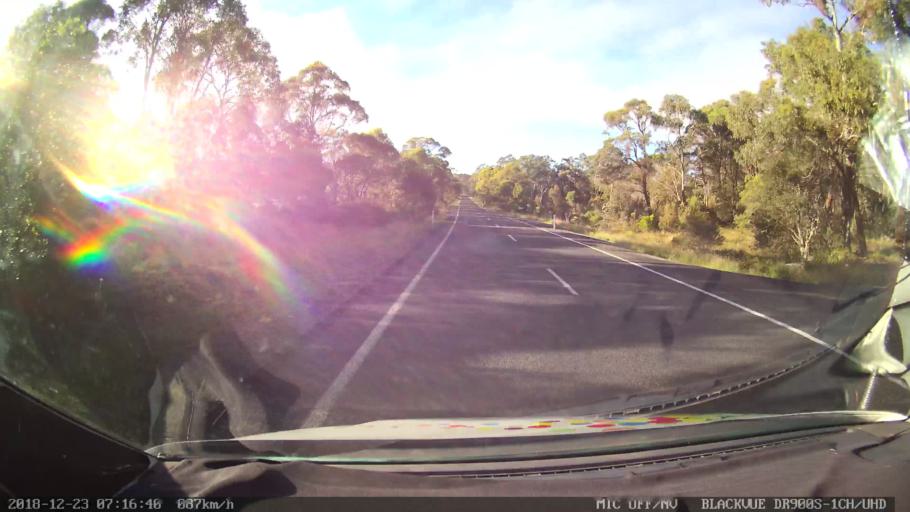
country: AU
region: New South Wales
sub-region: Bellingen
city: Dorrigo
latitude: -30.4587
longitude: 152.3083
